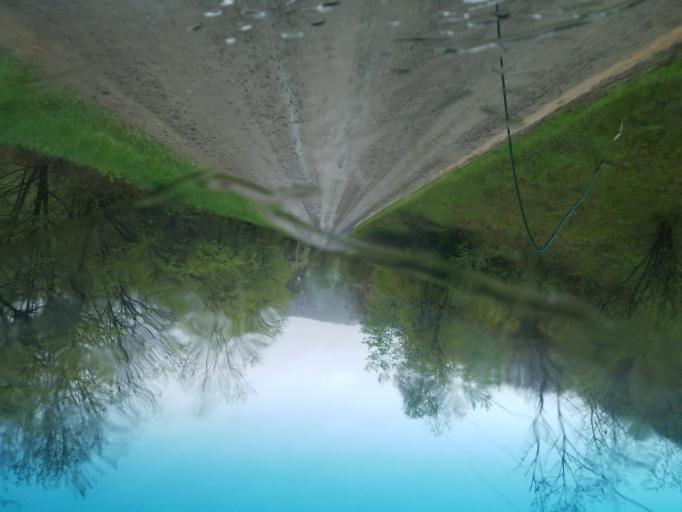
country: US
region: Pennsylvania
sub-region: Tioga County
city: Westfield
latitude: 41.9139
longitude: -77.6300
